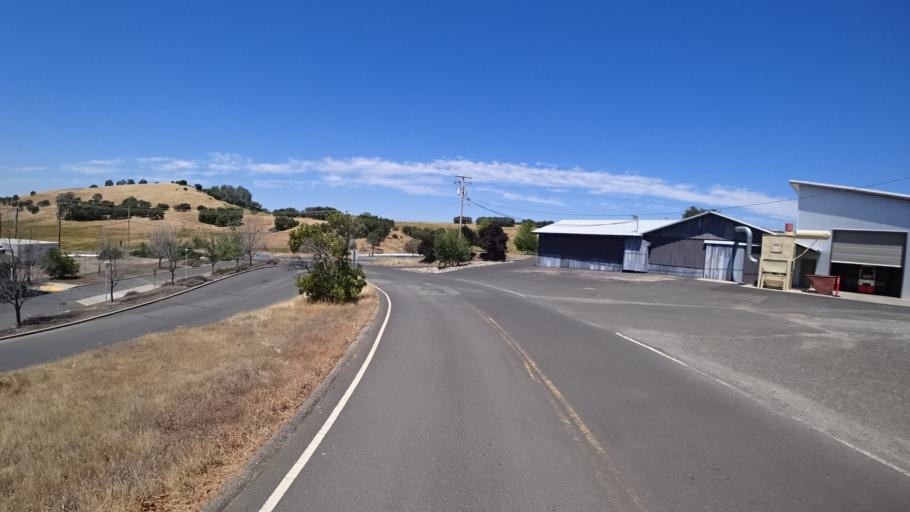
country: US
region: California
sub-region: Calaveras County
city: Angels Camp
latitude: 38.0861
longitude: -120.5392
